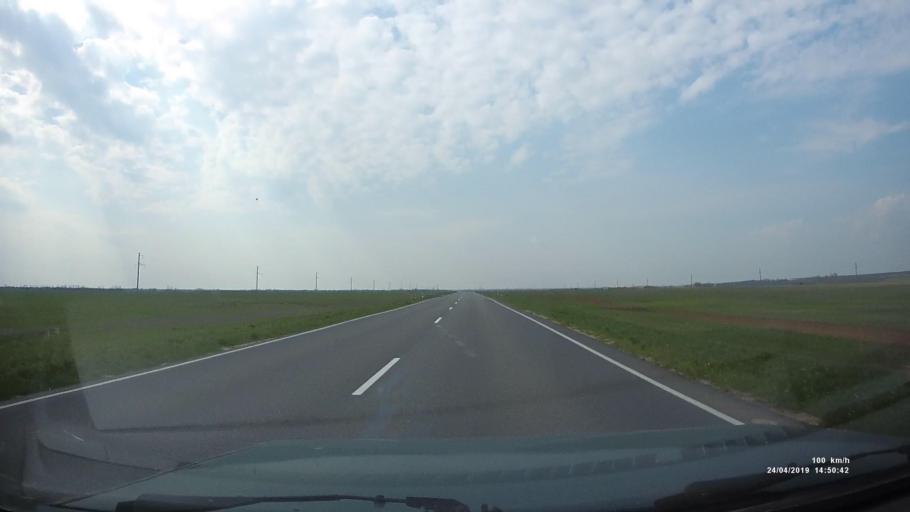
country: RU
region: Rostov
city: Remontnoye
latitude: 46.5193
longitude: 43.7147
